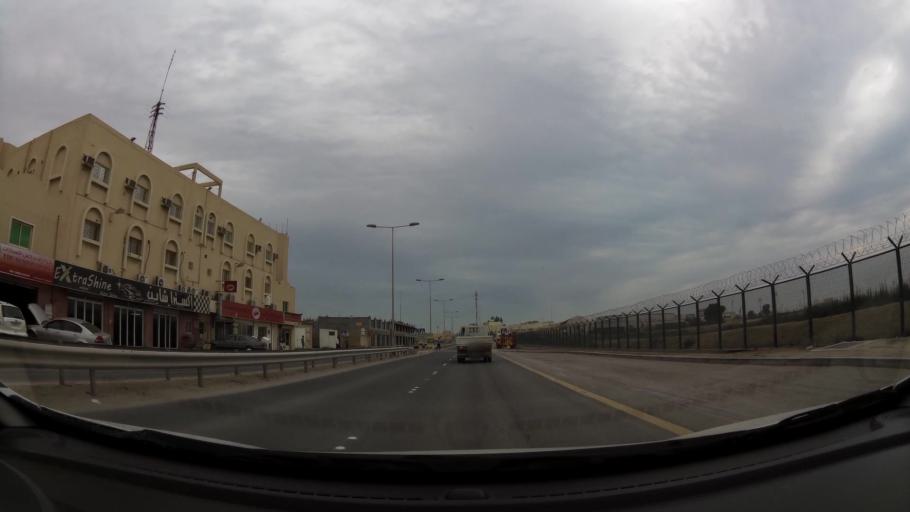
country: BH
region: Northern
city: Sitrah
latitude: 26.1519
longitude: 50.6205
